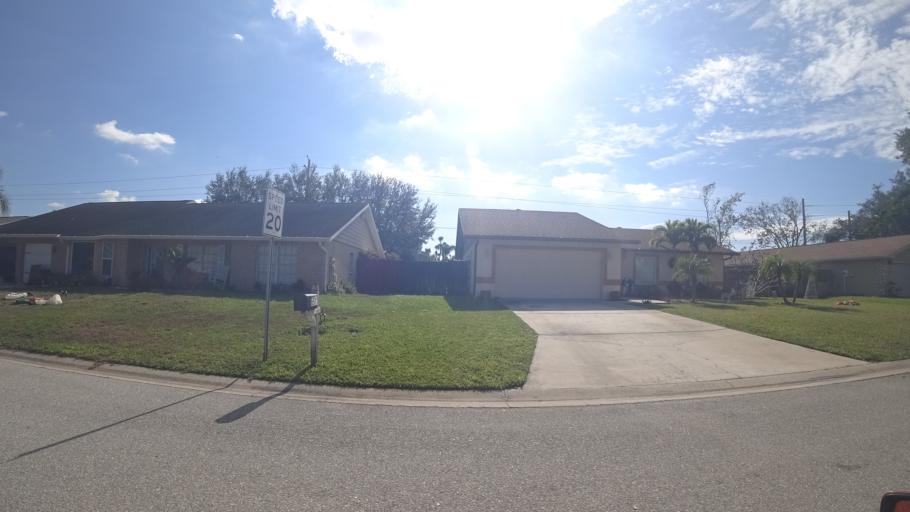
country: US
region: Florida
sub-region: Manatee County
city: West Bradenton
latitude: 27.5002
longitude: -82.6316
